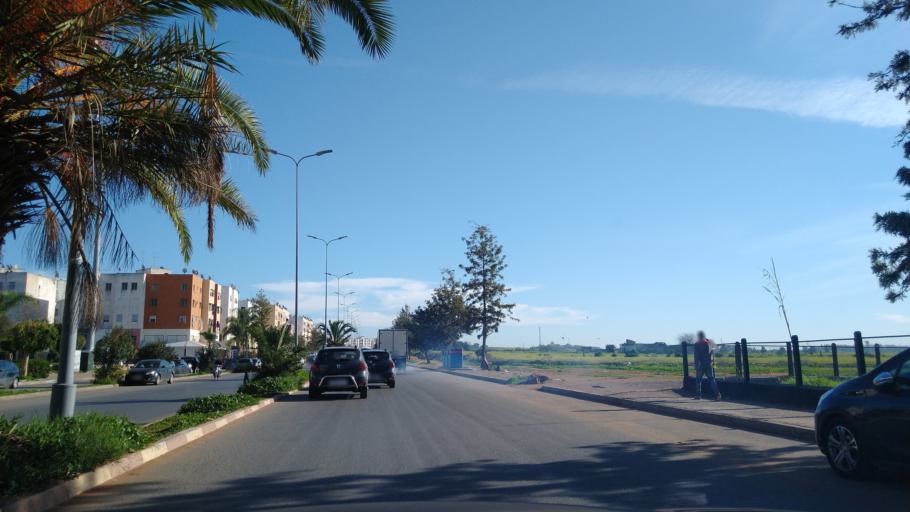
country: MA
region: Rabat-Sale-Zemmour-Zaer
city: Sale
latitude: 33.9937
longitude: -6.7444
